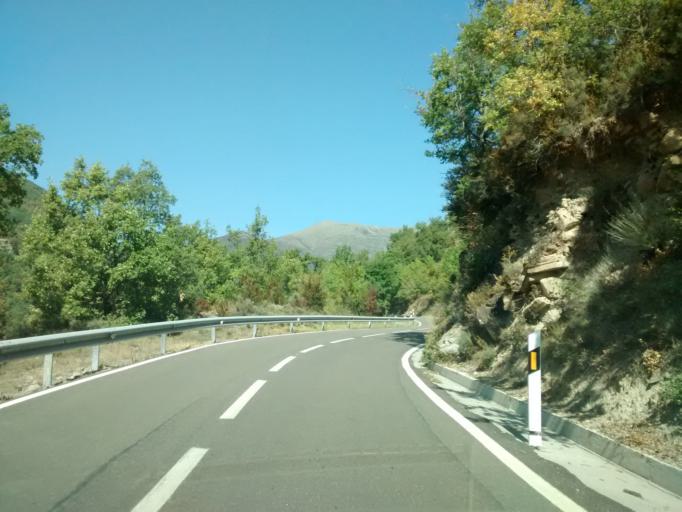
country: ES
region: Aragon
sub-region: Provincia de Huesca
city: Fiscal
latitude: 42.5178
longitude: -0.1281
